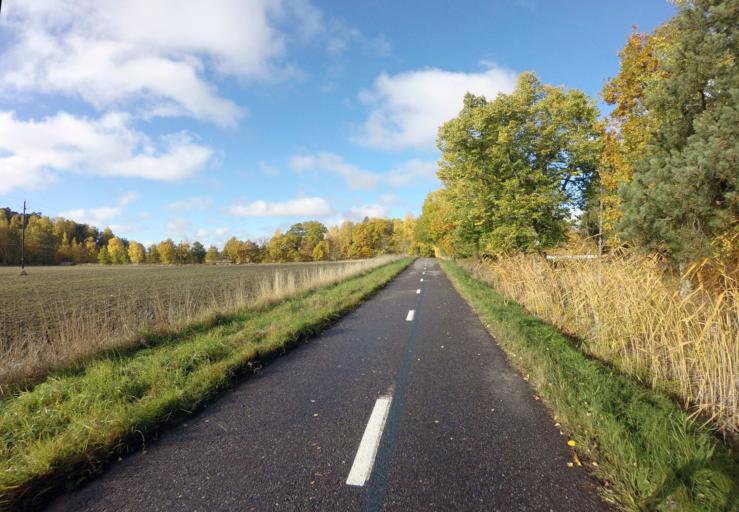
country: FI
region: Varsinais-Suomi
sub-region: Turku
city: Raisio
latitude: 60.4267
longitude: 22.1443
